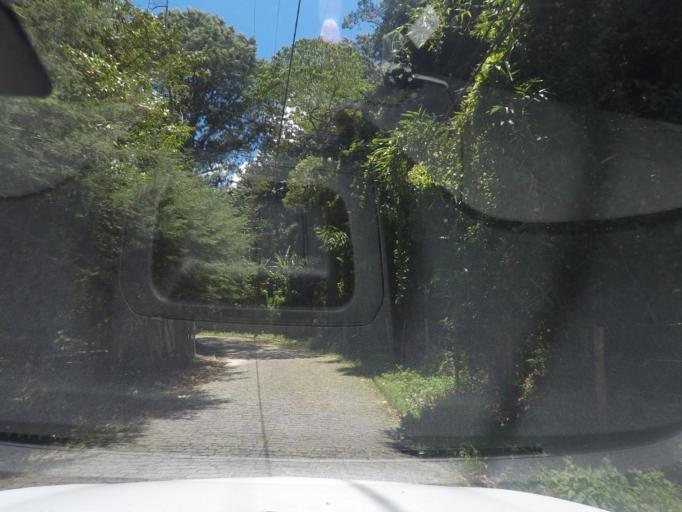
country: BR
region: Rio de Janeiro
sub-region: Teresopolis
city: Teresopolis
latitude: -22.4332
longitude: -42.9924
